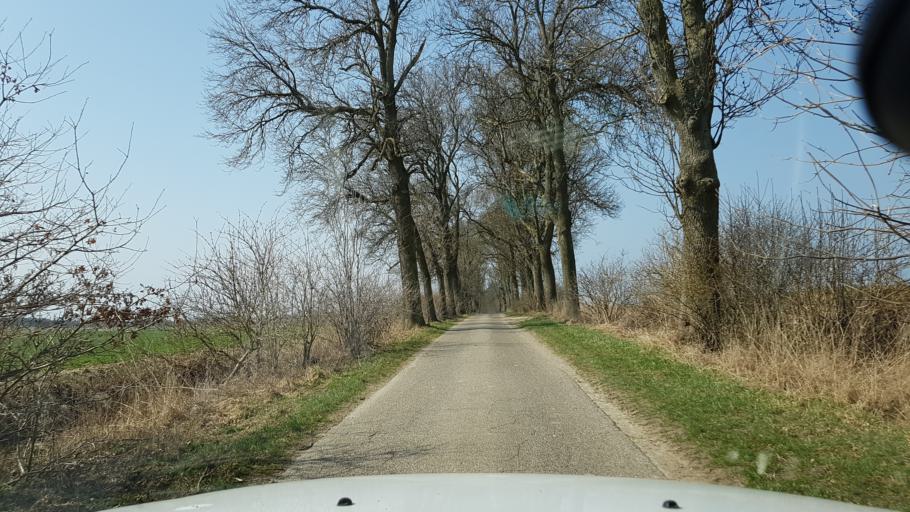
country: PL
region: West Pomeranian Voivodeship
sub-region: Powiat slawienski
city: Darlowo
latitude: 54.4690
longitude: 16.4861
